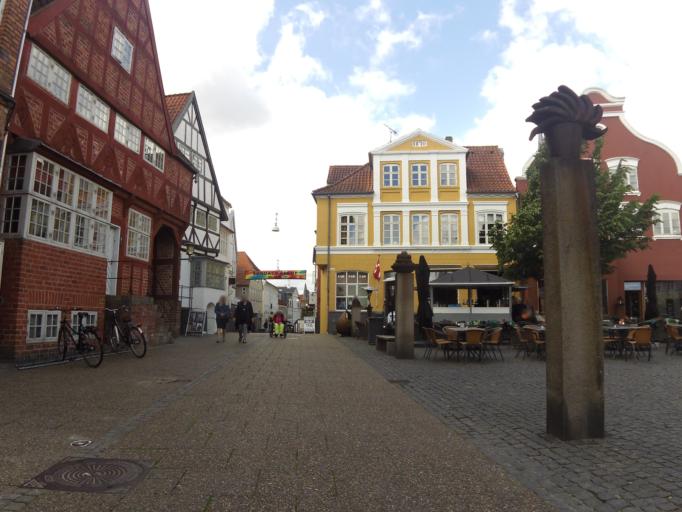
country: DK
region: South Denmark
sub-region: Haderslev Kommune
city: Haderslev
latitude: 55.2489
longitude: 9.4878
